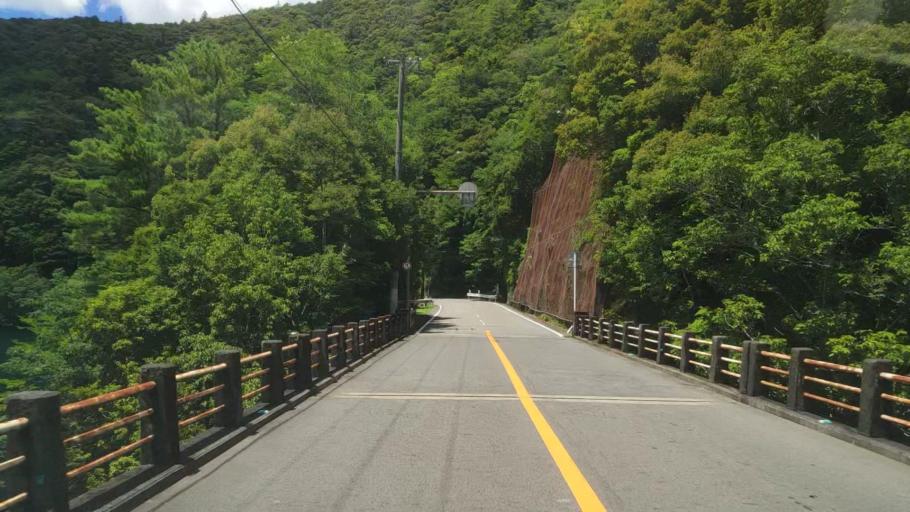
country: JP
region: Mie
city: Owase
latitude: 33.9985
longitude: 136.0170
